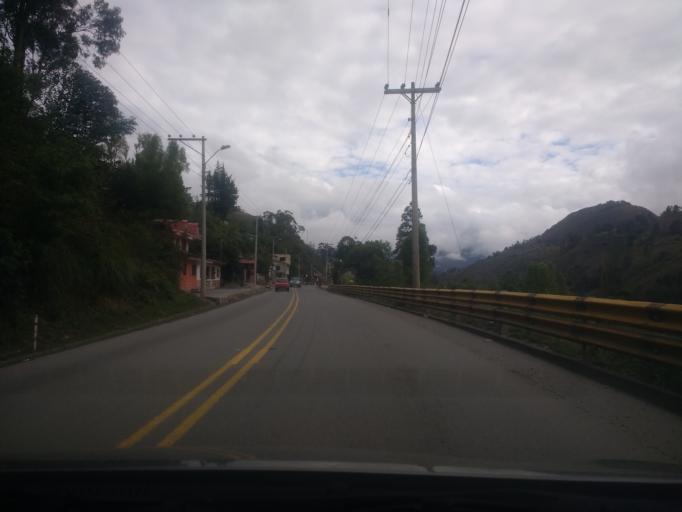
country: EC
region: Azuay
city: La Union
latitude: -2.8287
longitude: -78.7714
